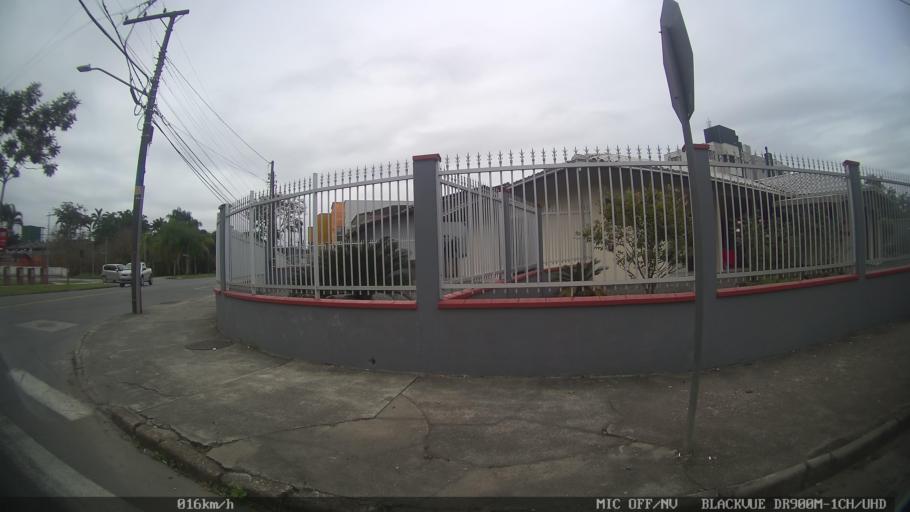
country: BR
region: Santa Catarina
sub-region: Joinville
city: Joinville
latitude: -26.2686
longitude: -48.8681
